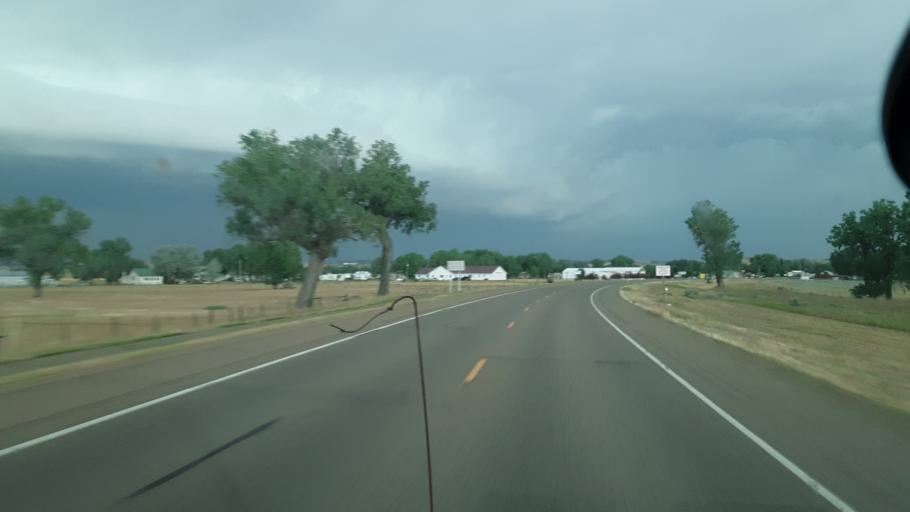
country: US
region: Montana
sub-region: Powder River County
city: Broadus
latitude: 45.4304
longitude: -105.4069
